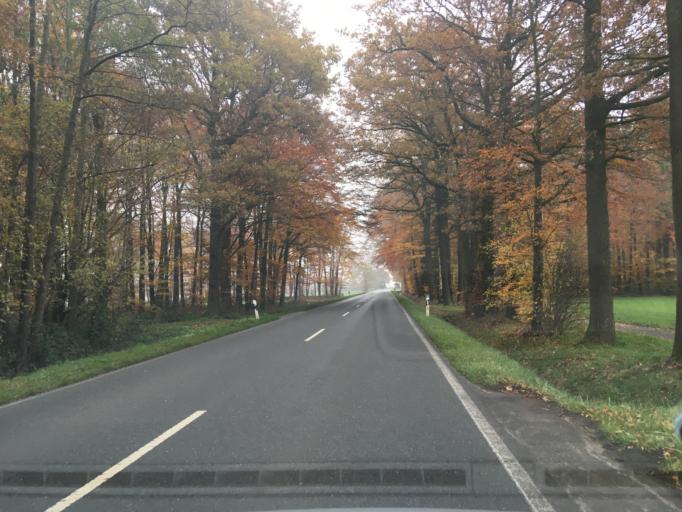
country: DE
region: North Rhine-Westphalia
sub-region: Regierungsbezirk Munster
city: Gescher
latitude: 51.9897
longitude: 6.9805
